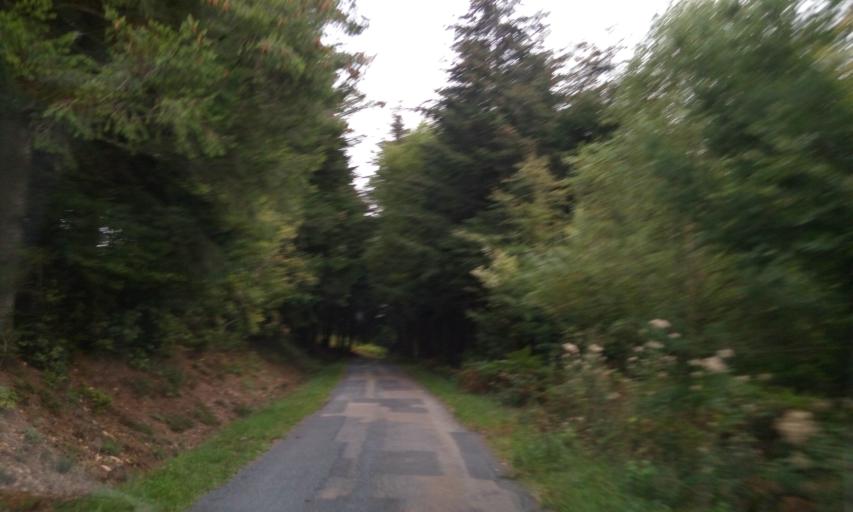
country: FR
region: Rhone-Alpes
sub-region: Departement du Rhone
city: Cublize
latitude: 46.0002
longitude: 4.4159
